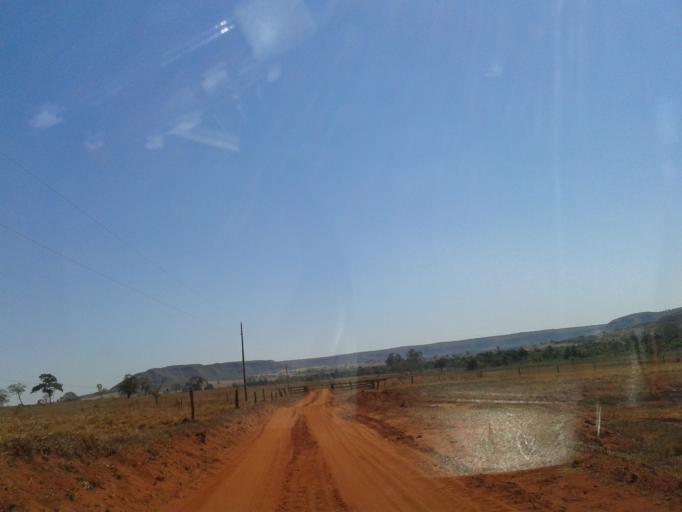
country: BR
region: Minas Gerais
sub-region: Santa Vitoria
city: Santa Vitoria
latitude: -19.0720
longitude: -50.0411
